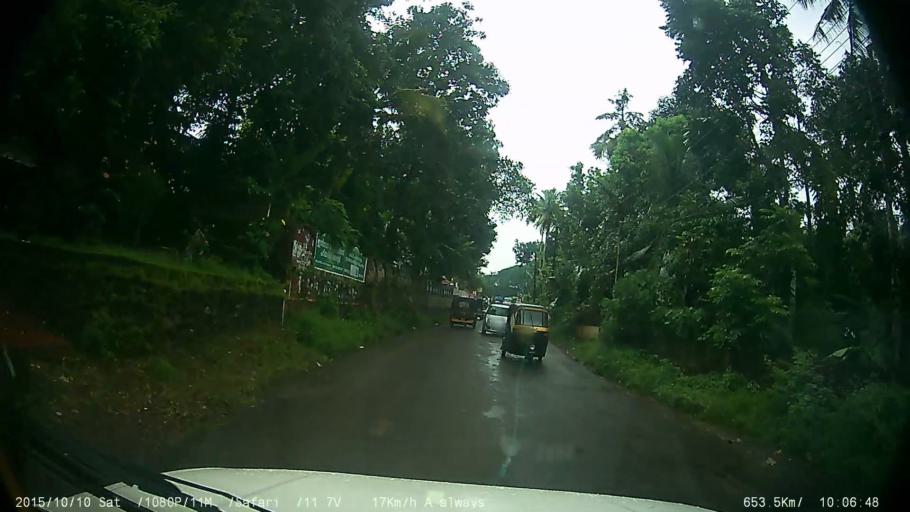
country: IN
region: Kerala
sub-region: Kottayam
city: Kottayam
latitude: 9.6414
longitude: 76.5334
